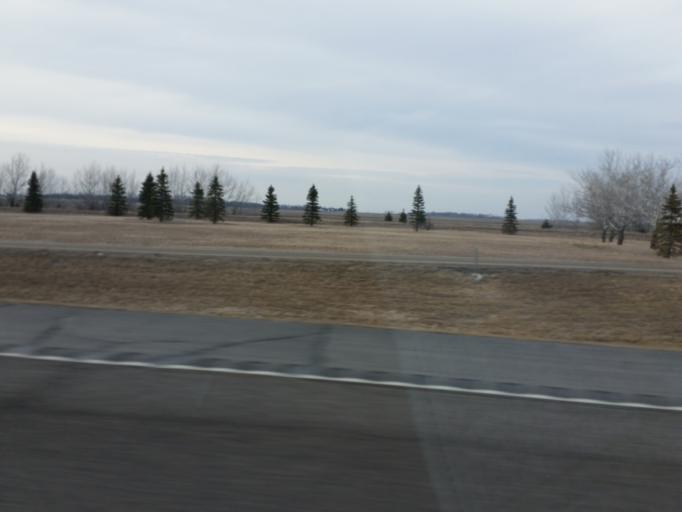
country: US
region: North Dakota
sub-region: Cass County
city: Casselton
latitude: 46.8770
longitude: -97.0902
